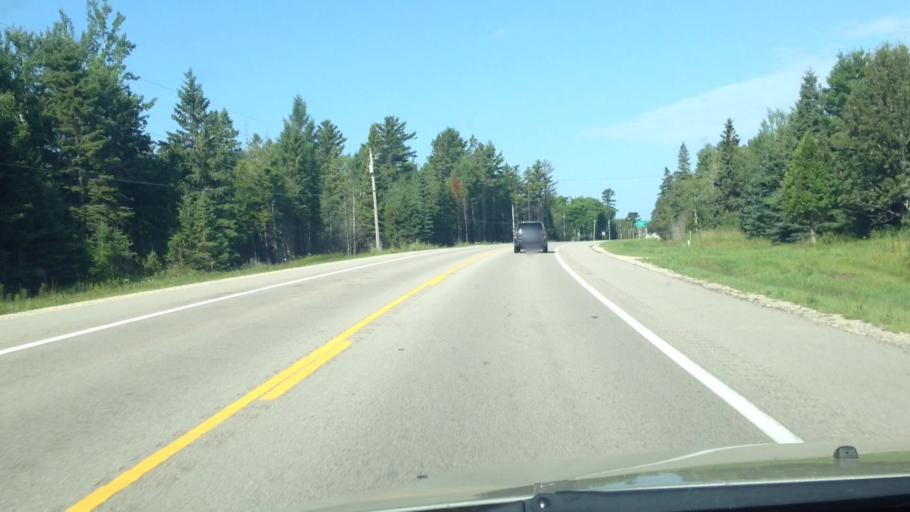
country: US
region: Michigan
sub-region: Schoolcraft County
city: Manistique
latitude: 45.9035
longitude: -86.3356
